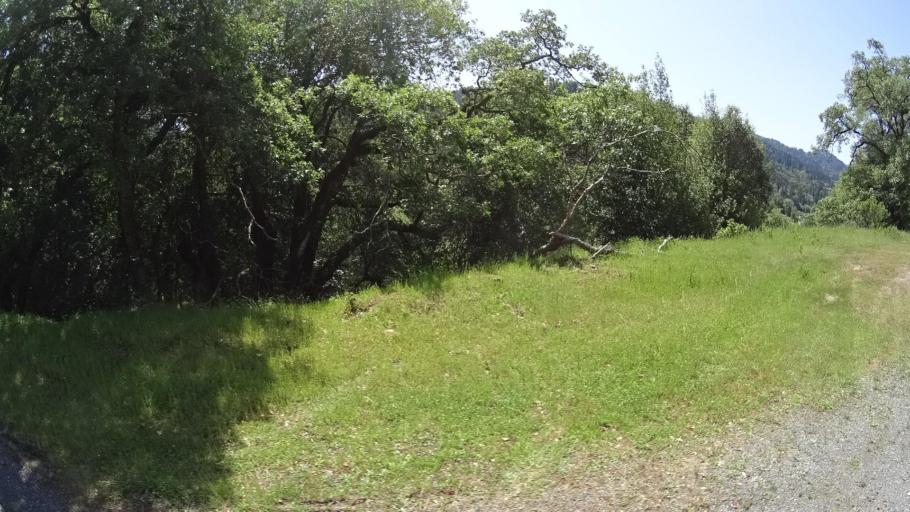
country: US
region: California
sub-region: Humboldt County
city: Redway
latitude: 40.2273
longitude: -123.6429
